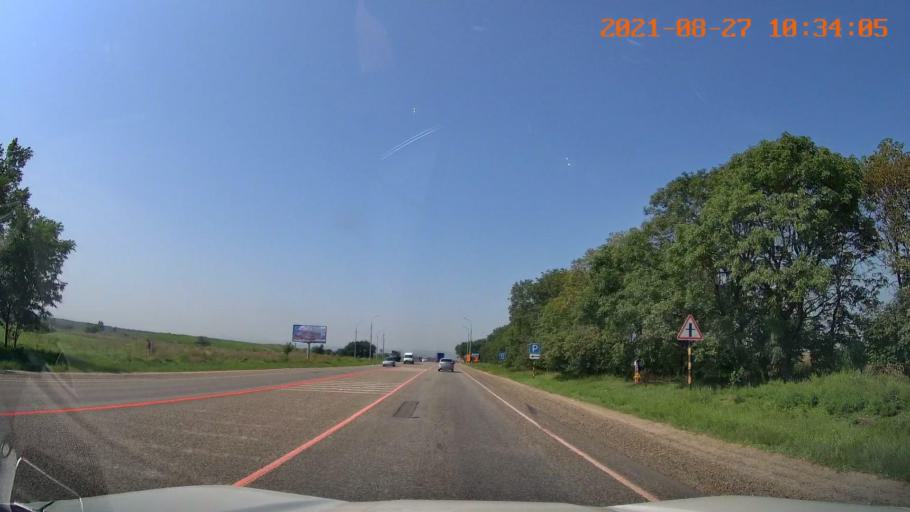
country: RU
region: Karachayevo-Cherkesiya
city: Cherkessk
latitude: 44.2561
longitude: 42.1118
